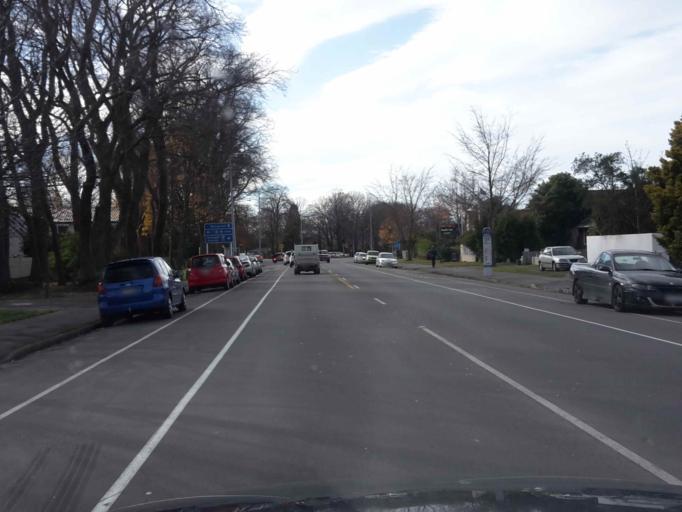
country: NZ
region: Canterbury
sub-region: Christchurch City
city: Christchurch
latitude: -43.5333
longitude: 172.5652
